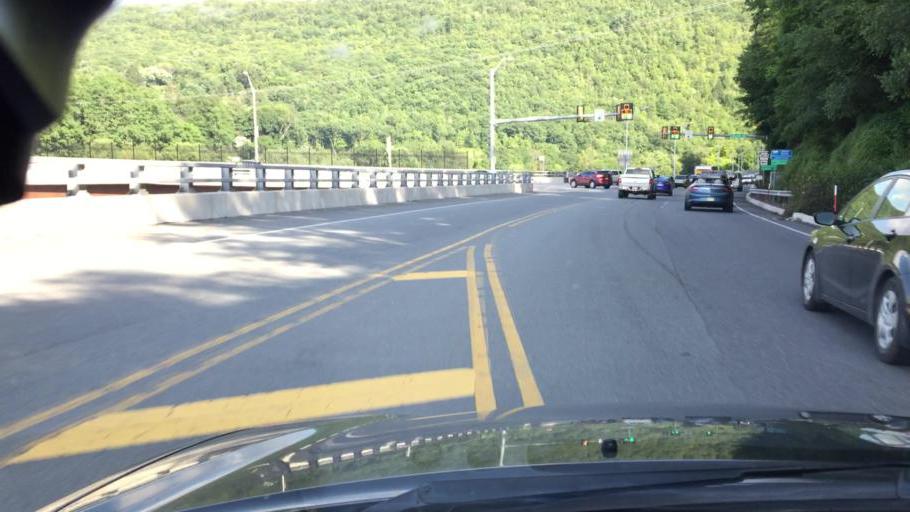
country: US
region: Pennsylvania
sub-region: Carbon County
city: Jim Thorpe
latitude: 40.8693
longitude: -75.7395
